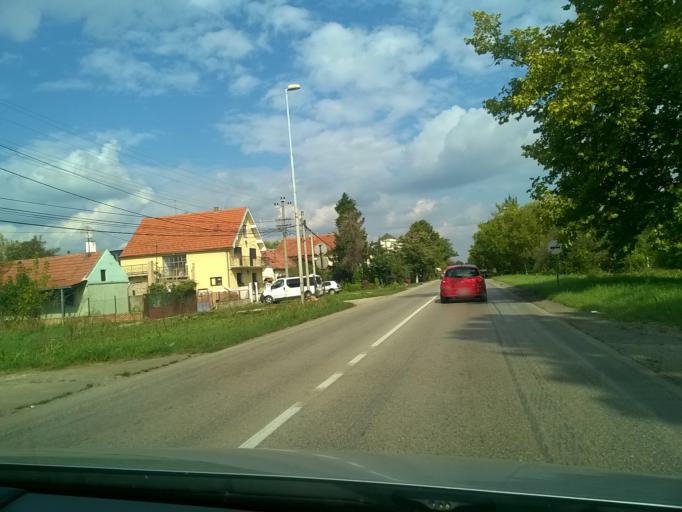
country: RS
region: Autonomna Pokrajina Vojvodina
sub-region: Juznobanatski Okrug
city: Pancevo
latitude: 44.8944
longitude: 20.6313
